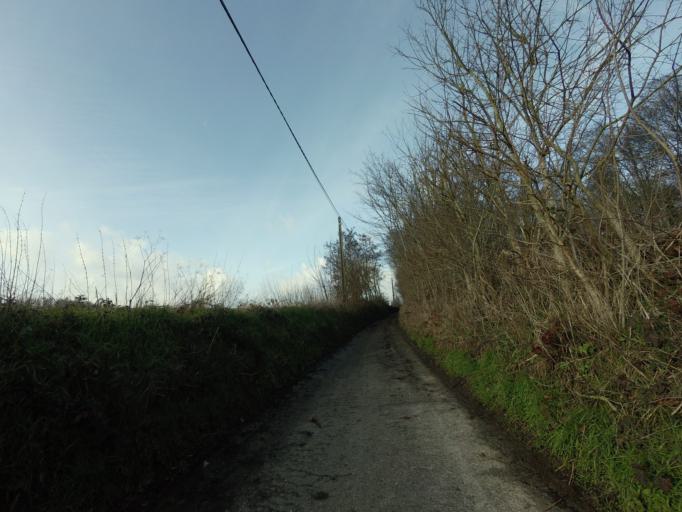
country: BE
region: Flanders
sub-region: Provincie Vlaams-Brabant
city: Bertem
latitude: 50.8807
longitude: 4.6065
